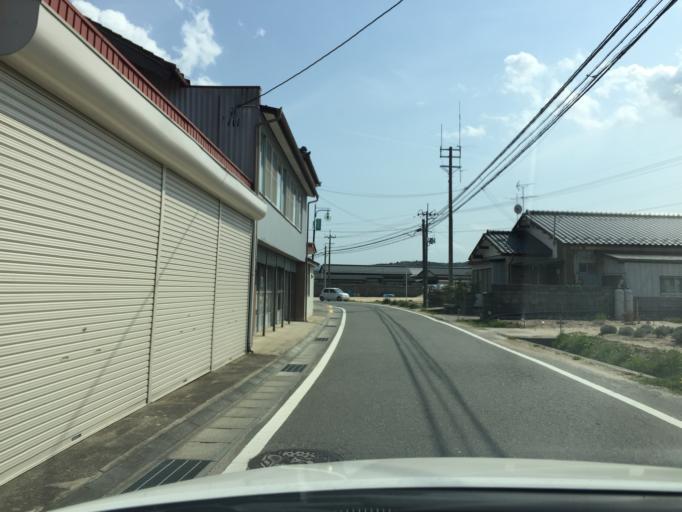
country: JP
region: Fukushima
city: Namie
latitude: 37.3271
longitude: 140.8345
